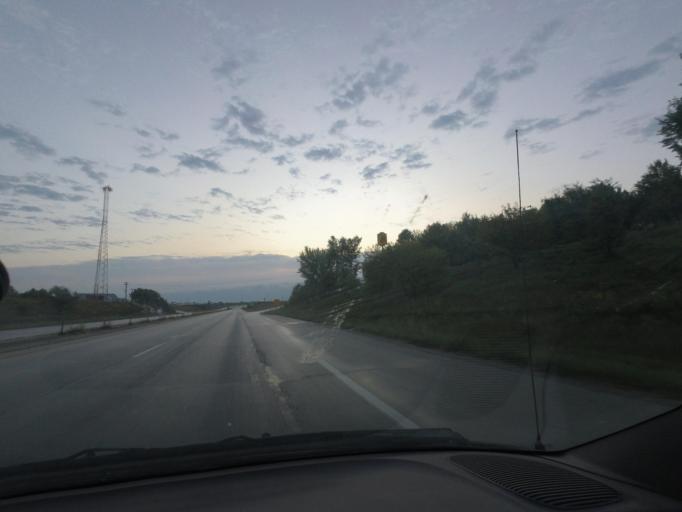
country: US
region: Missouri
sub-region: Macon County
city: Macon
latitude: 39.7529
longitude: -92.4713
